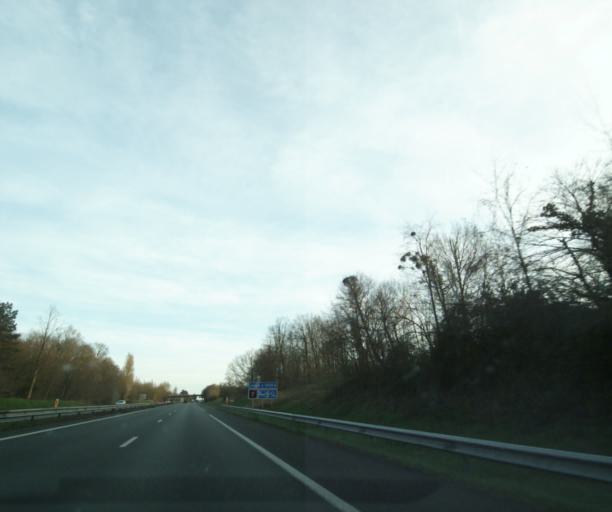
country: FR
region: Aquitaine
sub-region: Departement de la Gironde
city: Peujard
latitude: 45.0333
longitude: -0.4416
